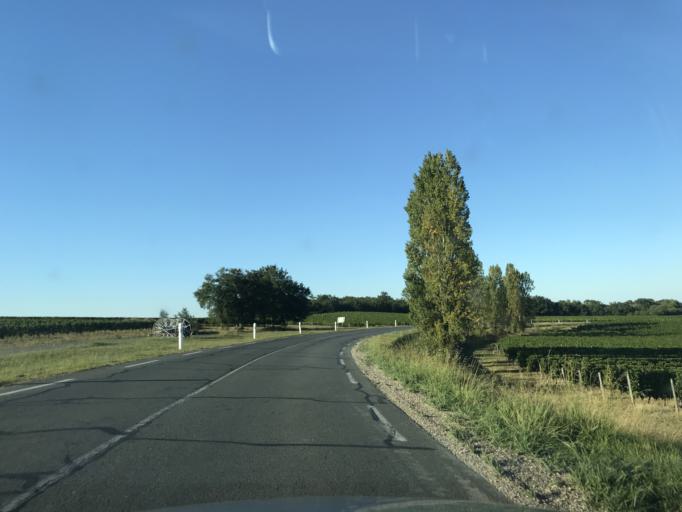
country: FR
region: Aquitaine
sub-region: Departement de la Gironde
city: Castets-en-Dorthe
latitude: 44.6191
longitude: -0.1644
